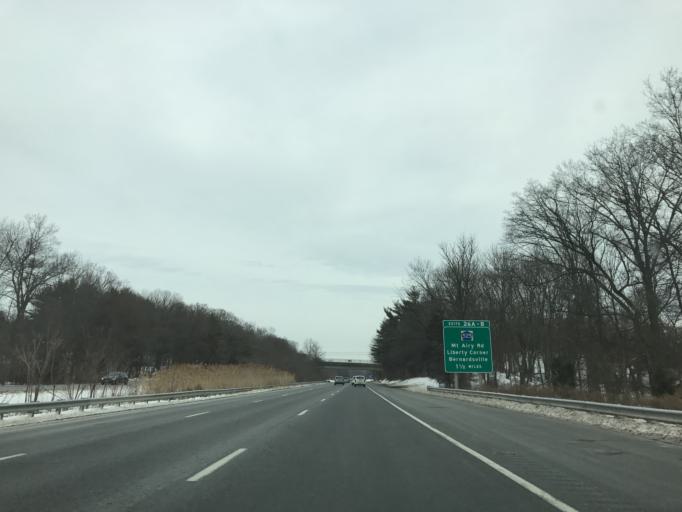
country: US
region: New Jersey
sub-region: Somerset County
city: Bedminster
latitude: 40.6767
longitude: -74.6045
